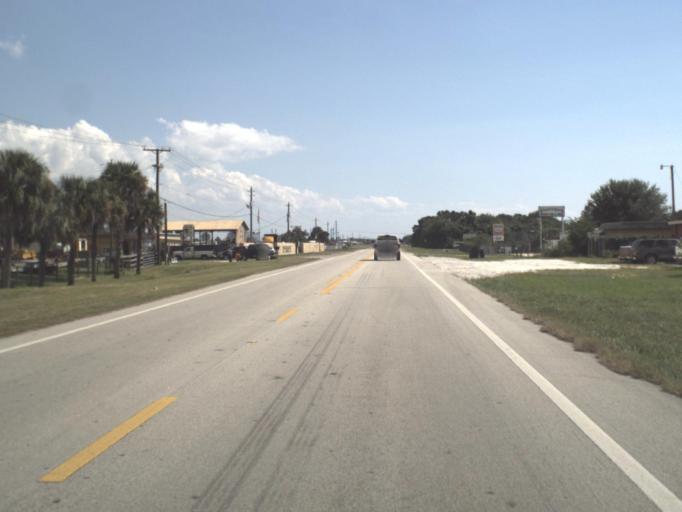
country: US
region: Florida
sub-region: Okeechobee County
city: Okeechobee
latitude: 27.2651
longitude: -80.8647
